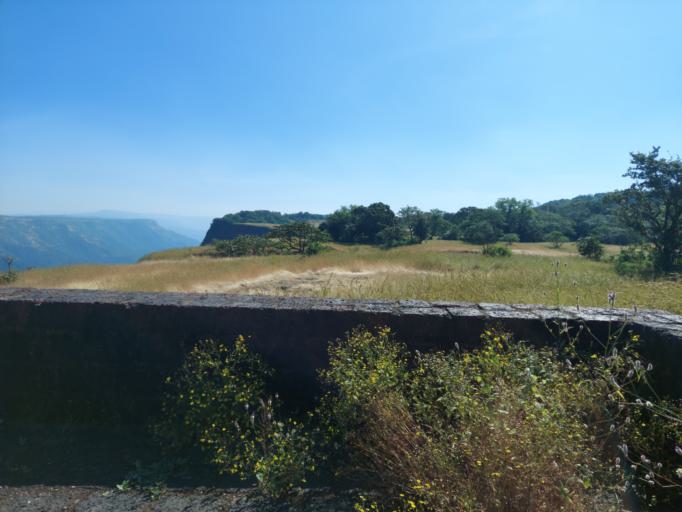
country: IN
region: Maharashtra
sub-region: Sindhudurg
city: Kudal
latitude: 16.0822
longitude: 73.8480
